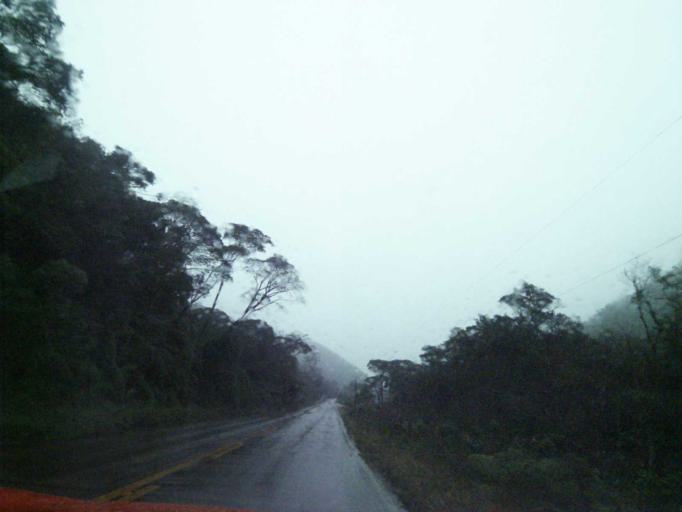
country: BR
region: Santa Catarina
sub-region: Anitapolis
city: Anitapolis
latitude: -27.7545
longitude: -49.0351
